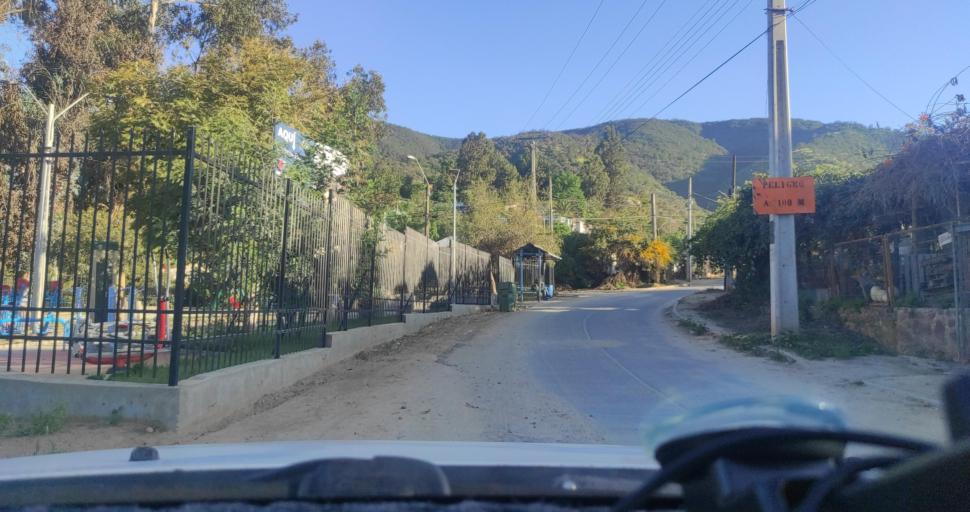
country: CL
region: Valparaiso
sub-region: Provincia de Marga Marga
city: Limache
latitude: -32.9886
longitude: -71.2359
